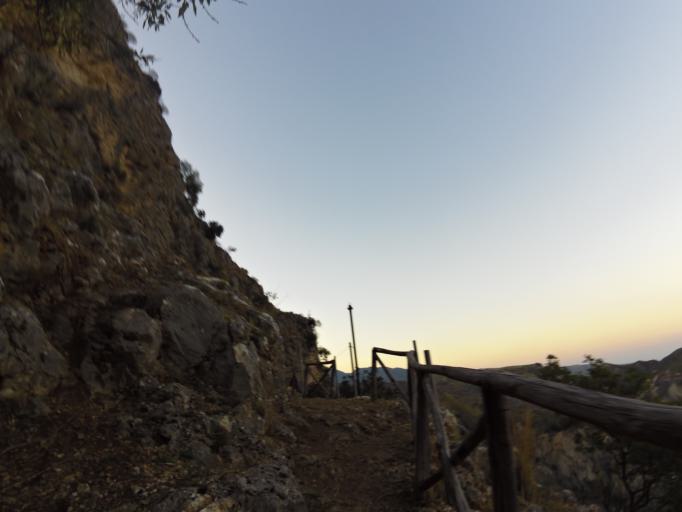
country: IT
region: Calabria
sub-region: Provincia di Reggio Calabria
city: Stilo
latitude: 38.4818
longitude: 16.4692
